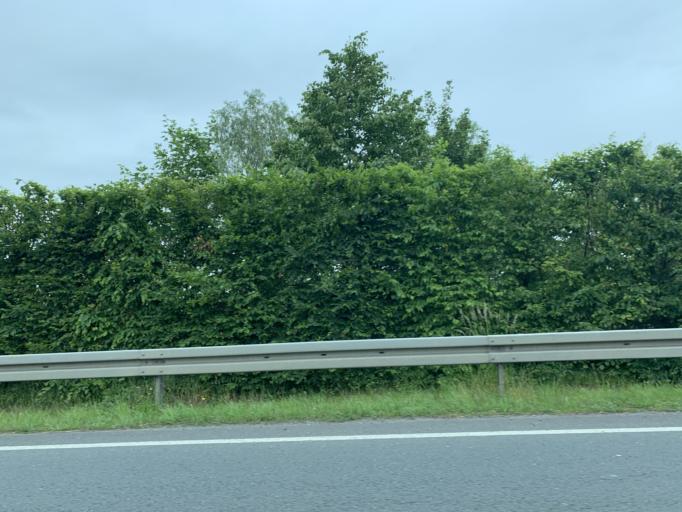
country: DE
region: North Rhine-Westphalia
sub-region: Regierungsbezirk Arnsberg
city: Hamm
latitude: 51.6605
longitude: 7.8377
